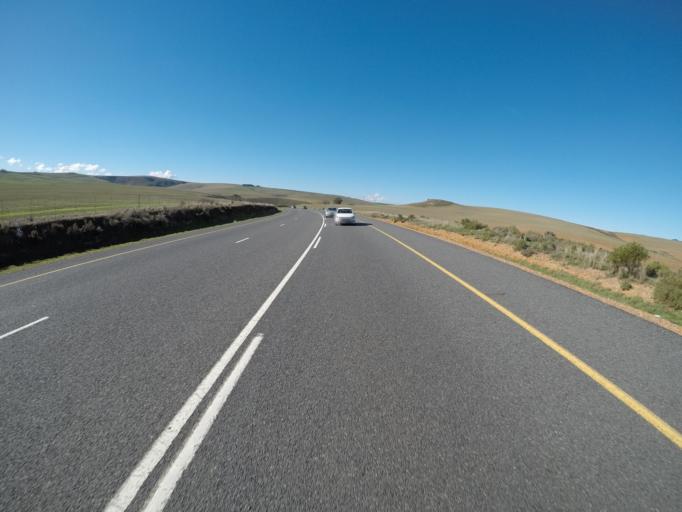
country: ZA
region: Western Cape
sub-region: Overberg District Municipality
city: Hermanus
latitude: -34.2339
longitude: 19.2339
